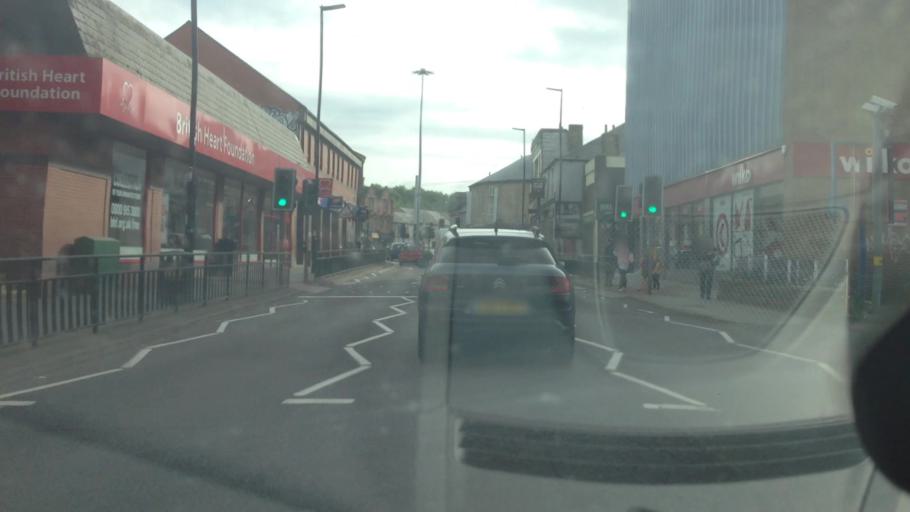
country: GB
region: England
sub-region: Sheffield
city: Sheffield
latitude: 53.4032
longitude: -1.5001
